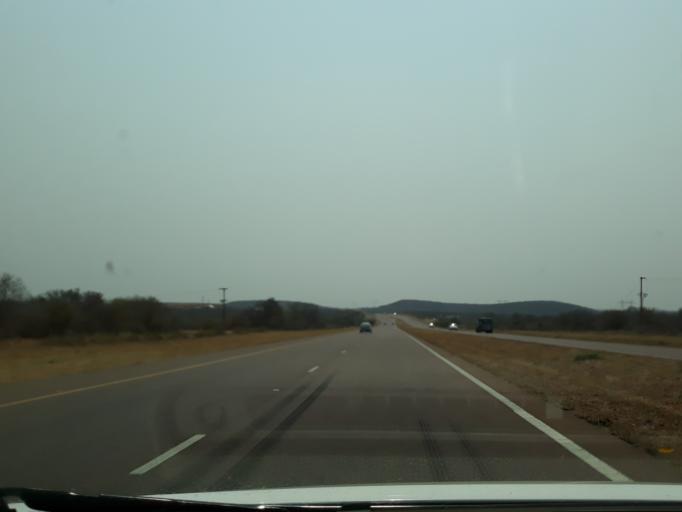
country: BW
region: Kgatleng
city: Bokaa
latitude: -24.4084
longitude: 26.0528
